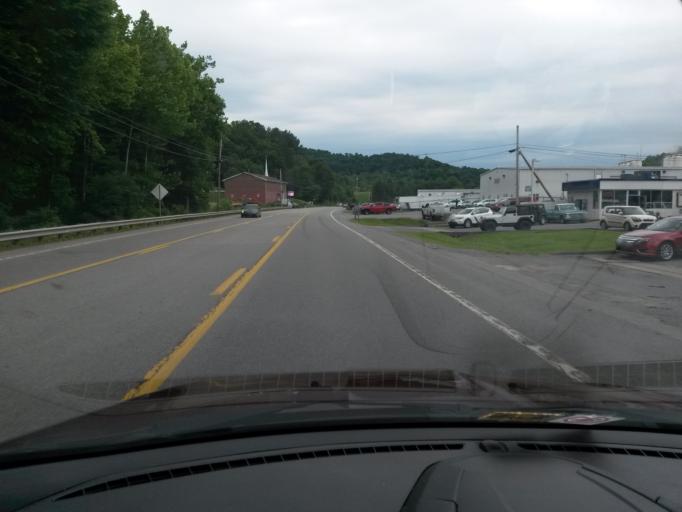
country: US
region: West Virginia
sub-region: Lewis County
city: Weston
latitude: 39.0332
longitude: -80.4427
